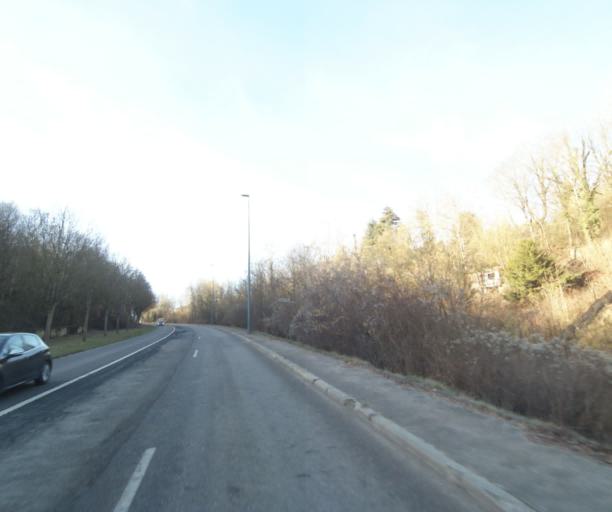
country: FR
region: Lorraine
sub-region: Departement de Meurthe-et-Moselle
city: Villers-les-Nancy
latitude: 48.6649
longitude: 6.1437
